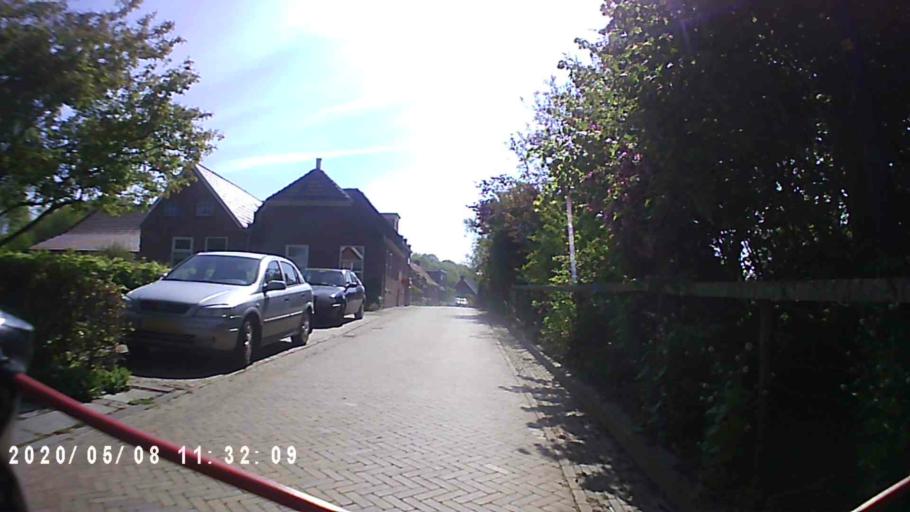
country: NL
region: Groningen
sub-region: Gemeente Bedum
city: Bedum
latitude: 53.3444
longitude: 6.7086
